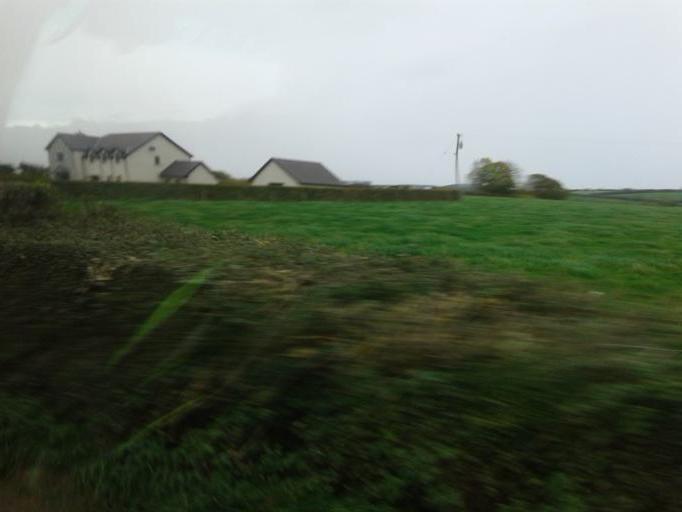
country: IE
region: Leinster
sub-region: Uibh Fhaili
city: Birr
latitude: 52.9750
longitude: -7.9862
